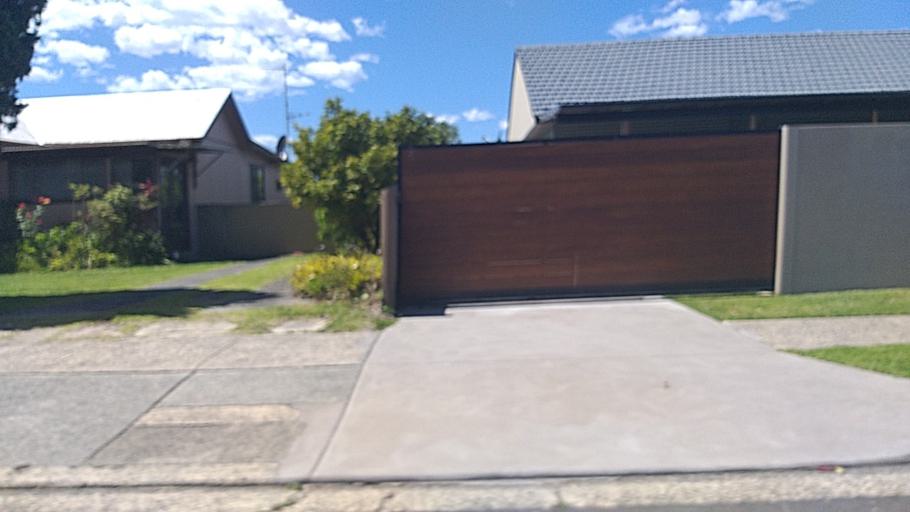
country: AU
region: New South Wales
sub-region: Wollongong
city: East Corrimal
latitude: -34.3781
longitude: 150.9083
